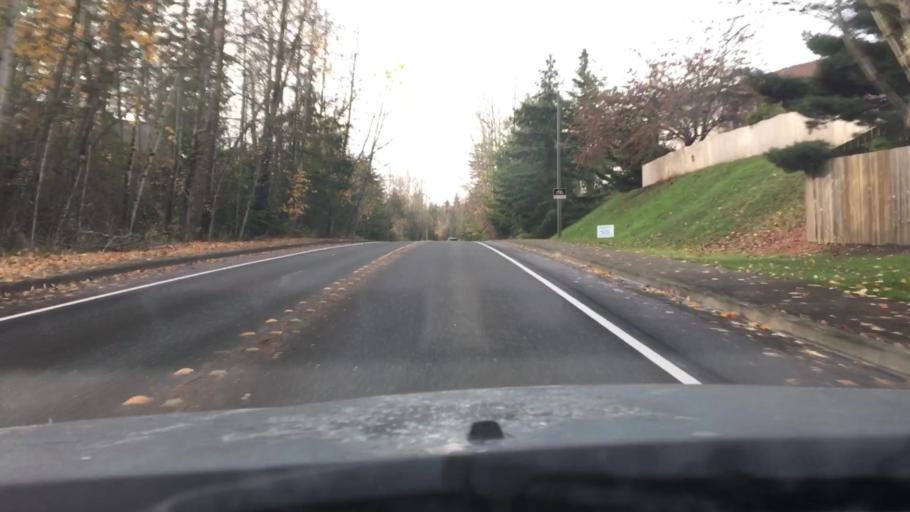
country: US
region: Washington
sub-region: Whatcom County
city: Geneva
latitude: 48.7728
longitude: -122.4139
